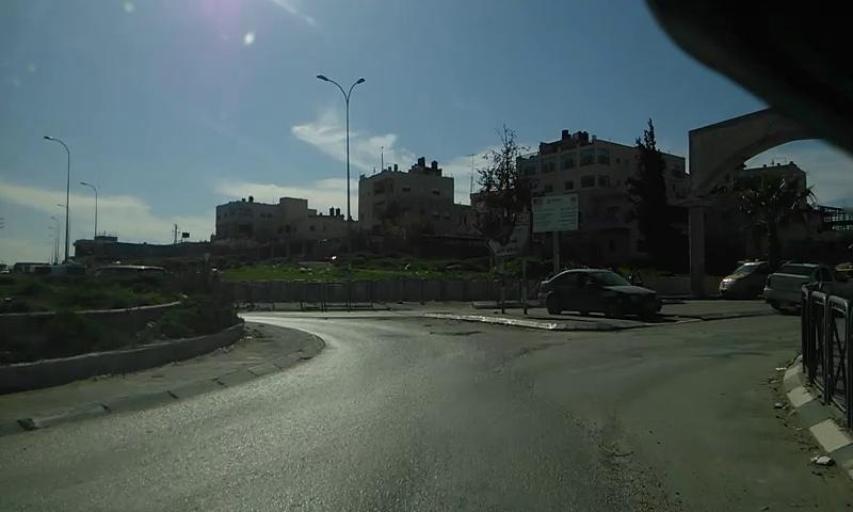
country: PS
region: West Bank
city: Ar Ram wa Dahiyat al Barid
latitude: 31.8563
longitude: 35.2405
